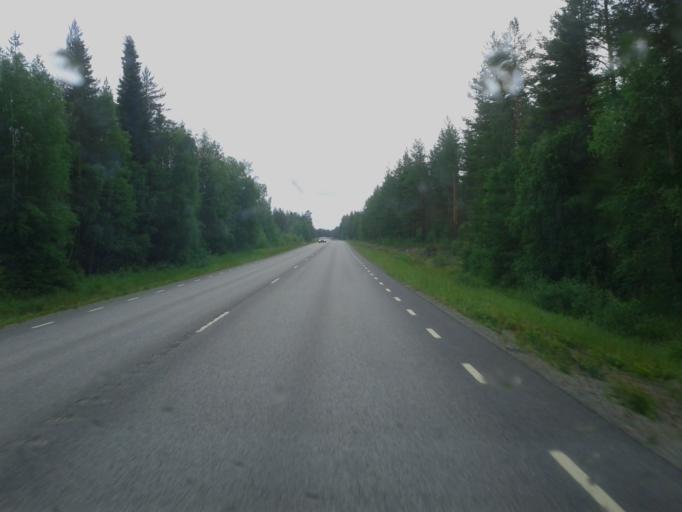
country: SE
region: Vaesterbotten
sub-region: Skelleftea Kommun
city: Langsele
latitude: 64.9433
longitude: 19.9272
